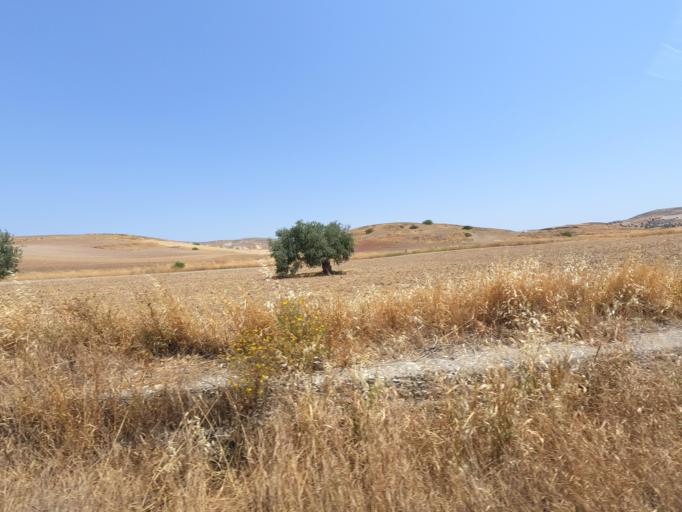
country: CY
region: Larnaka
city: Troulloi
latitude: 35.0251
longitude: 33.6331
